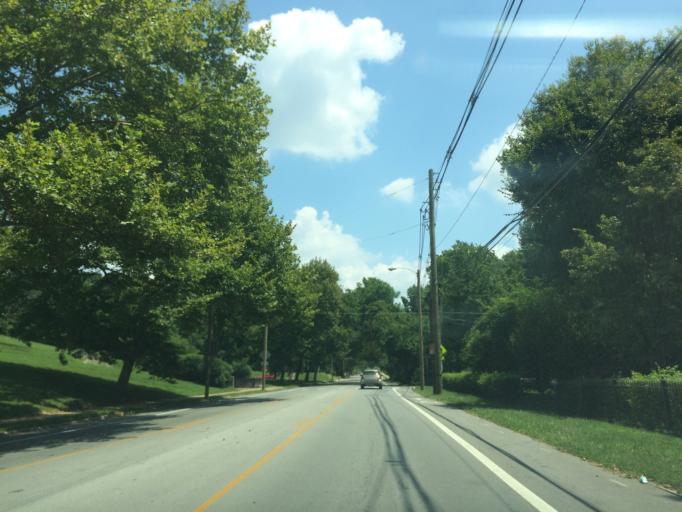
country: US
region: Kentucky
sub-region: Jefferson County
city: Saint Matthews
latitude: 38.2486
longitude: -85.6966
